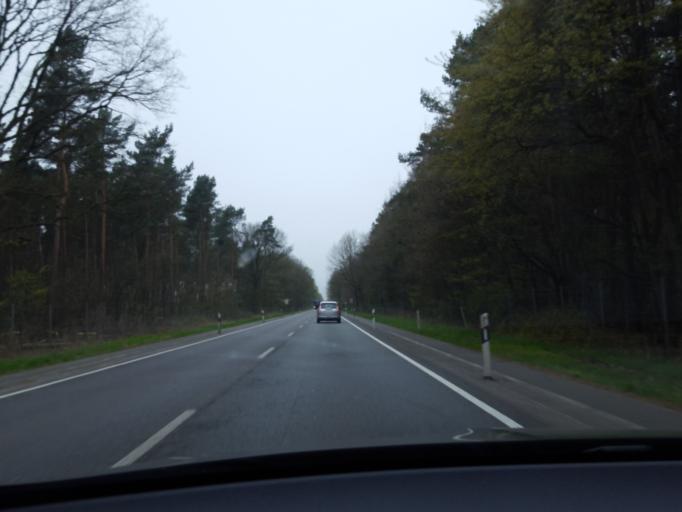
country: DE
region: North Rhine-Westphalia
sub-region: Regierungsbezirk Munster
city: Raesfeld
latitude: 51.7369
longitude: 6.8877
